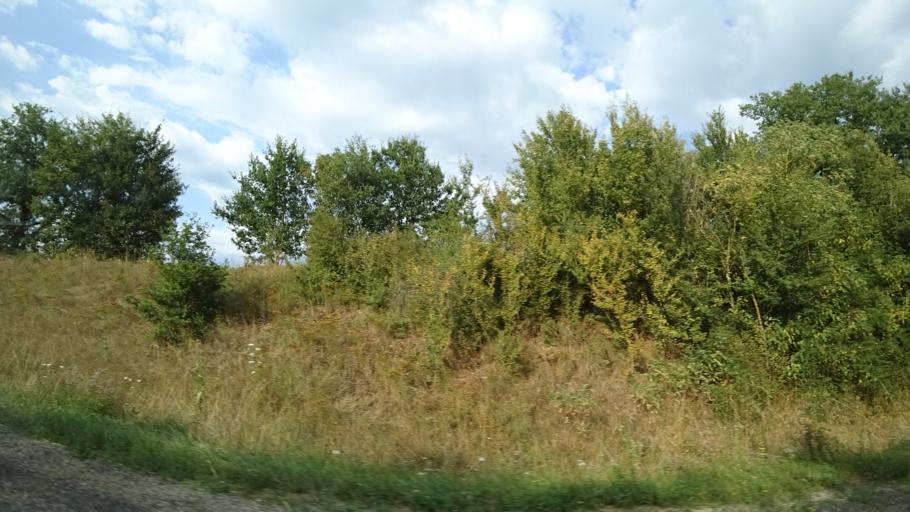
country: FR
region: Midi-Pyrenees
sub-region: Departement de l'Aveyron
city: Saint-Christophe-Vallon
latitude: 44.4781
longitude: 2.4066
